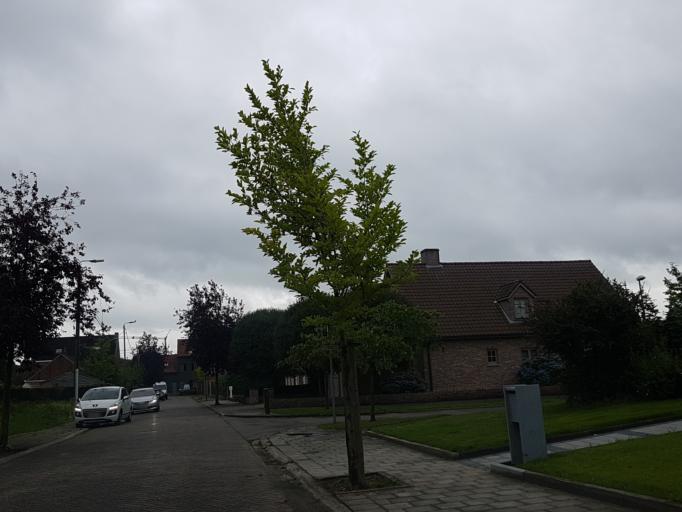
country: BE
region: Flanders
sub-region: Provincie Vlaams-Brabant
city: Zemst
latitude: 50.9650
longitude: 4.5027
